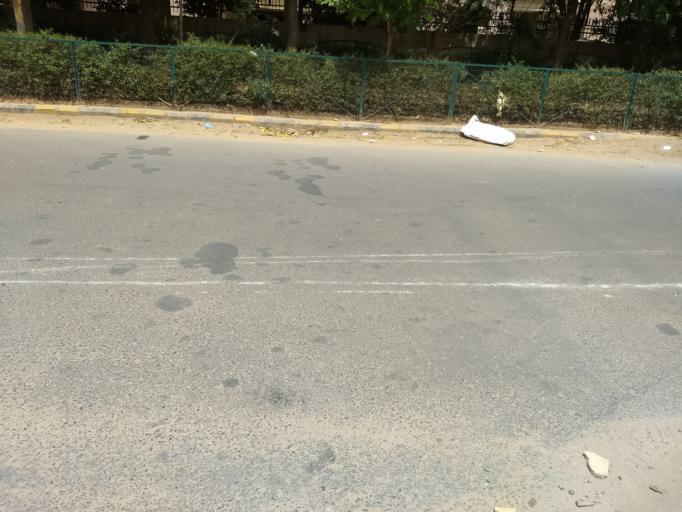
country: IN
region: Haryana
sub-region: Gurgaon
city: Gurgaon
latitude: 28.4547
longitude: 77.0948
